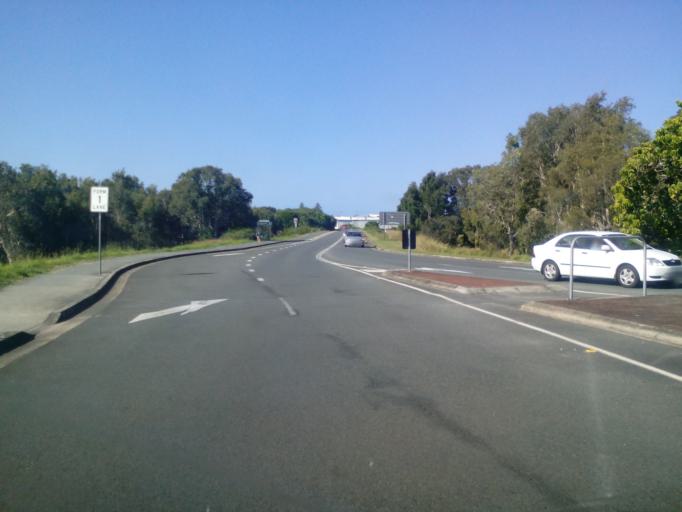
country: AU
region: New South Wales
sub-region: Tweed
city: Kingscliff
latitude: -28.2581
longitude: 153.5703
